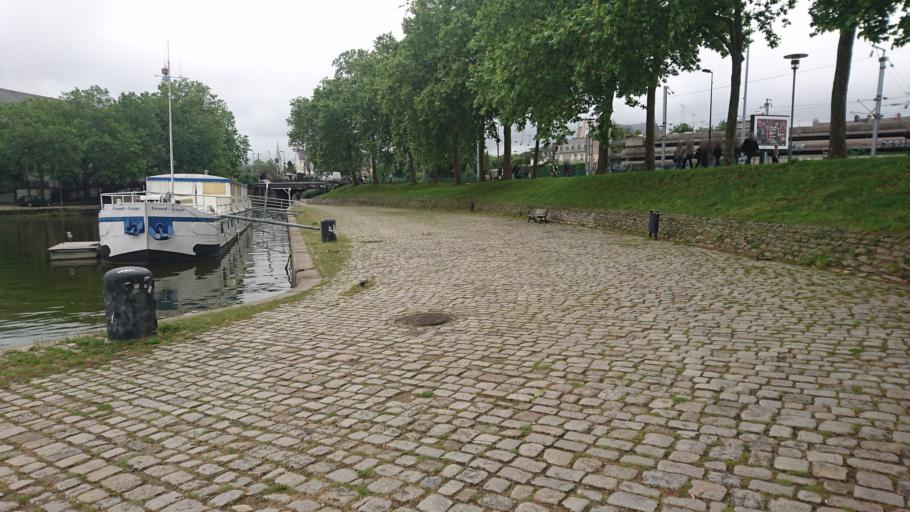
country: FR
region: Pays de la Loire
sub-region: Departement de la Loire-Atlantique
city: Nantes
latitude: 47.2158
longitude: -1.5437
